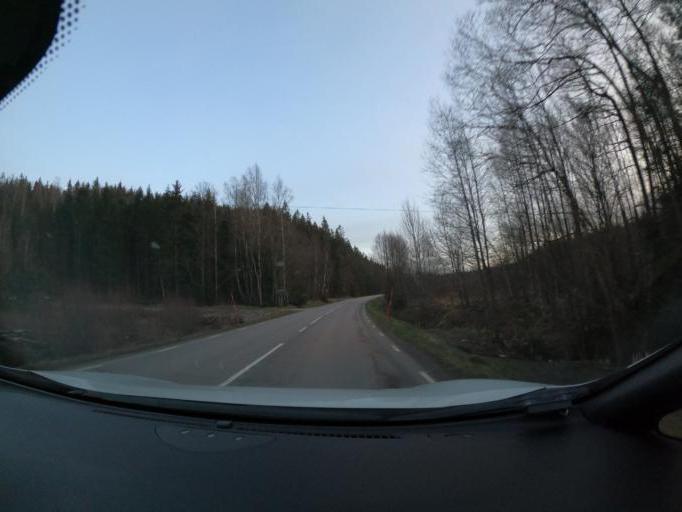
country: SE
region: Vaestra Goetaland
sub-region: Harryda Kommun
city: Landvetter
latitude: 57.6245
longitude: 12.1822
